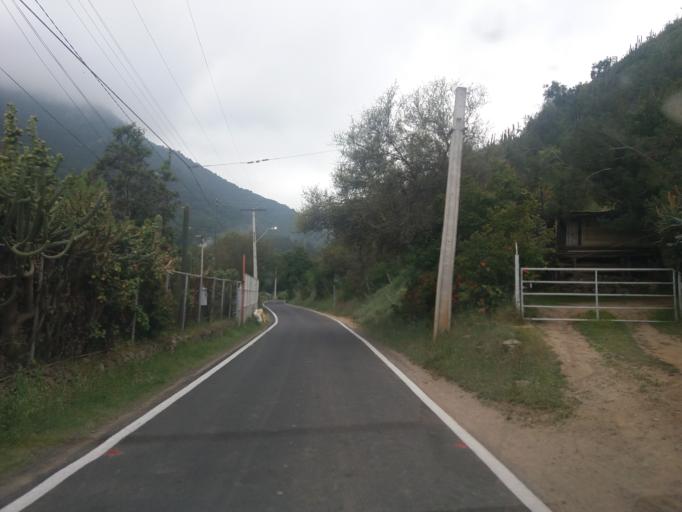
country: CL
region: Valparaiso
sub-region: Provincia de Marga Marga
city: Limache
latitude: -33.0408
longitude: -71.0964
